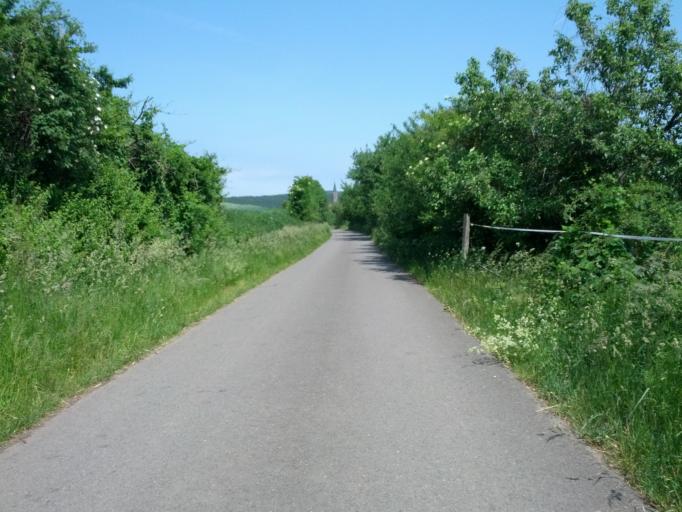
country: DE
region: Thuringia
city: Urnshausen
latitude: 50.7295
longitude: 10.1672
